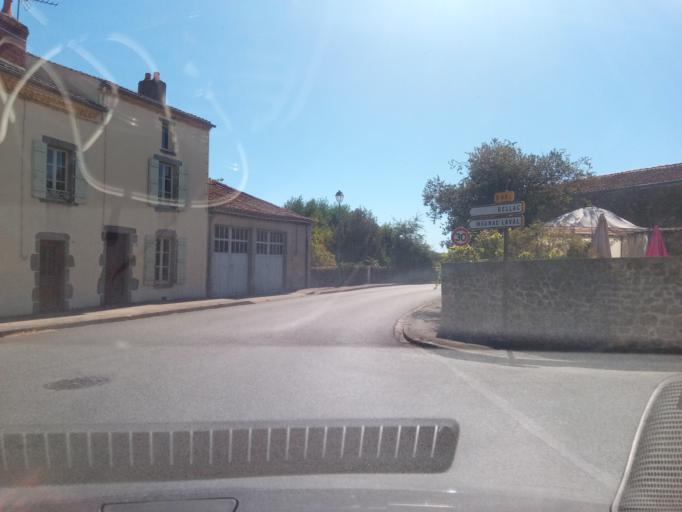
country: FR
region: Limousin
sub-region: Departement de la Haute-Vienne
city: Le Dorat
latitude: 46.2162
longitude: 1.0838
